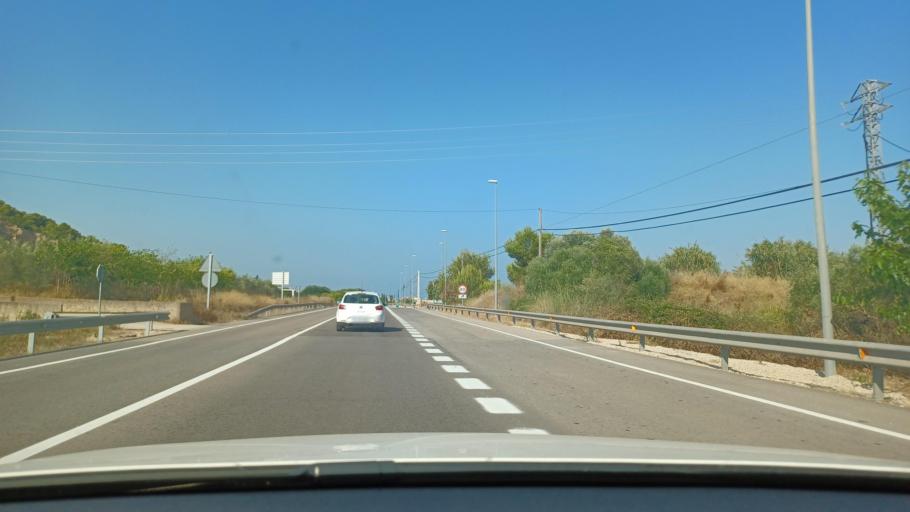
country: ES
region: Catalonia
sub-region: Provincia de Tarragona
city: Alcanar
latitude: 40.5576
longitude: 0.5278
